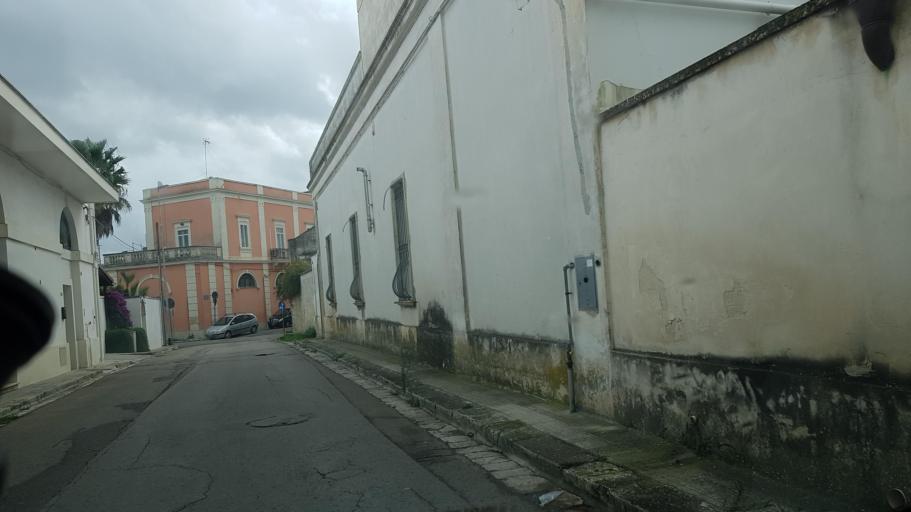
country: IT
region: Apulia
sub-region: Provincia di Lecce
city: Carmiano
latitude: 40.3473
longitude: 18.0493
